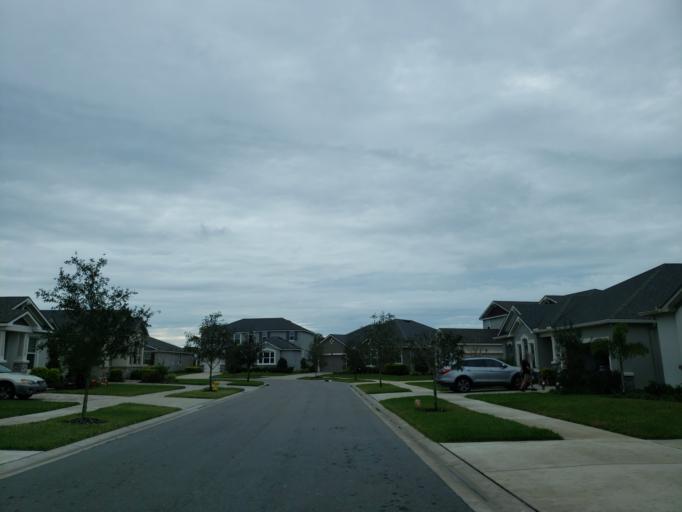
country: US
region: Florida
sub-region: Hillsborough County
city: Riverview
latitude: 27.8484
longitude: -82.3053
